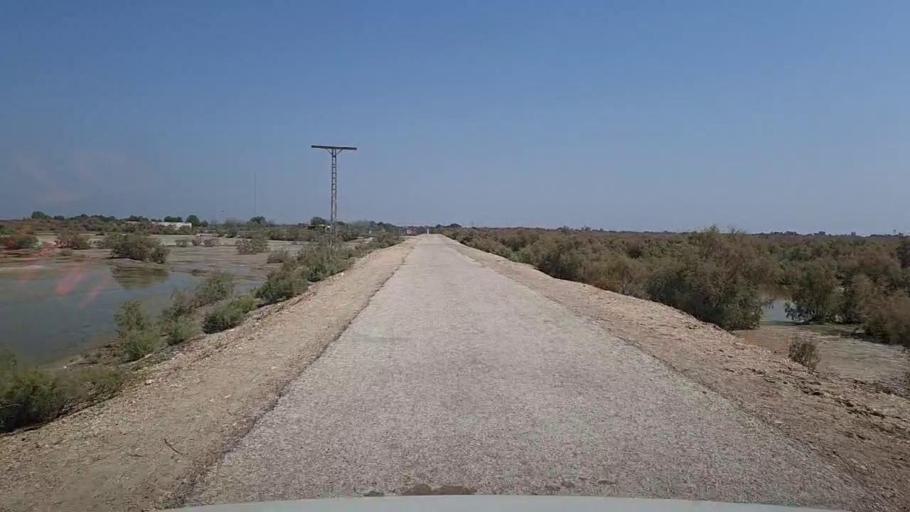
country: PK
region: Sindh
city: Kandhkot
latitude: 28.3031
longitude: 69.3475
